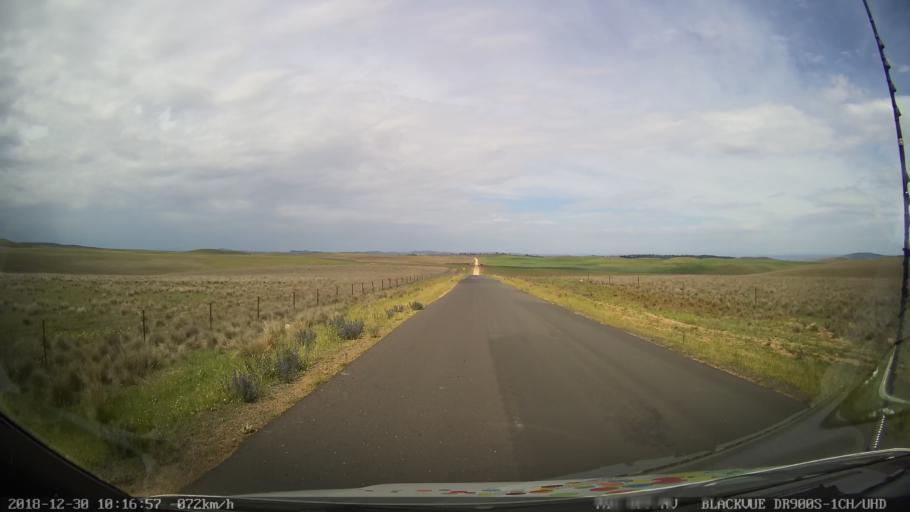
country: AU
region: New South Wales
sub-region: Snowy River
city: Berridale
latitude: -36.5469
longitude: 149.0273
